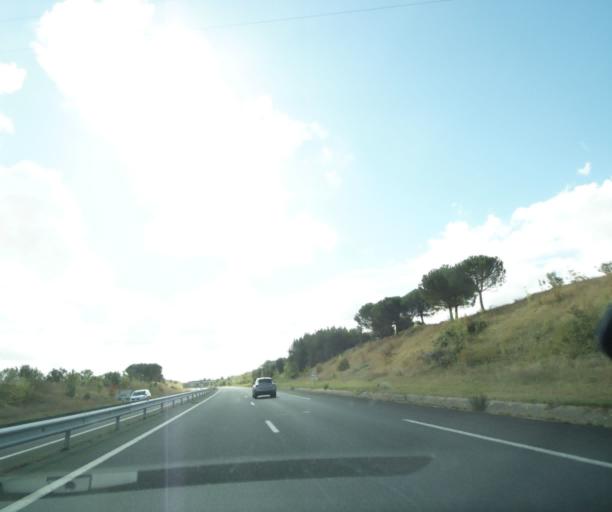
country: FR
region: Poitou-Charentes
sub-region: Departement de la Charente-Maritime
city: Saint-Savinien
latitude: 45.8577
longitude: -0.7289
